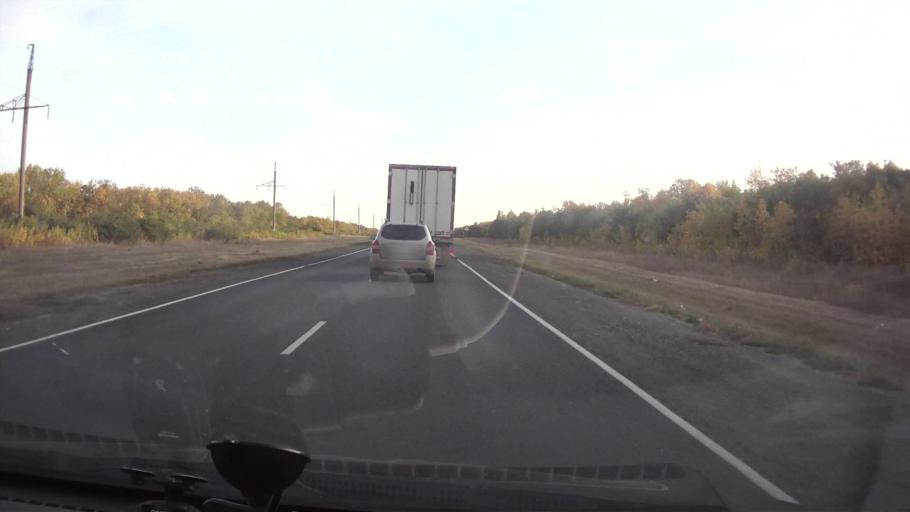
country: RU
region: Saratov
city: Krasnoarmeysk
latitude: 51.1309
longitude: 45.6504
